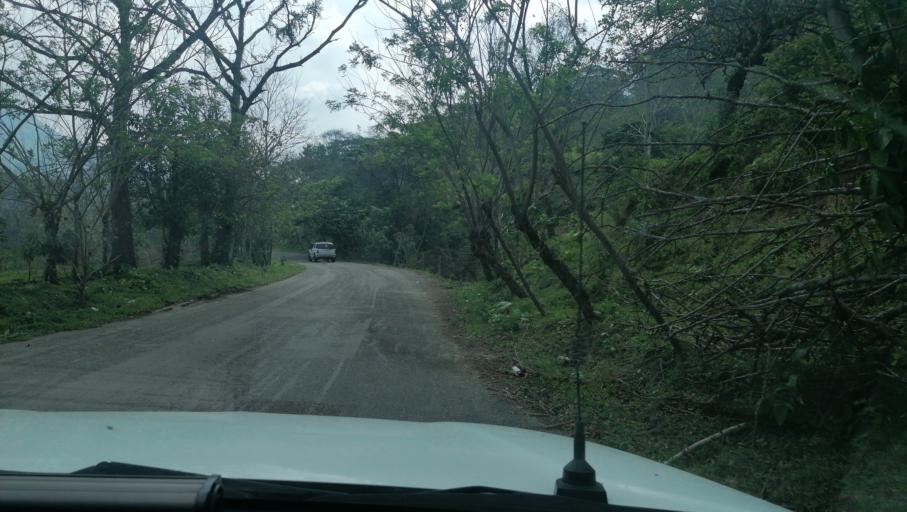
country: MX
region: Chiapas
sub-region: Francisco Leon
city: San Miguel la Sardina
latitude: 17.2280
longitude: -93.3438
